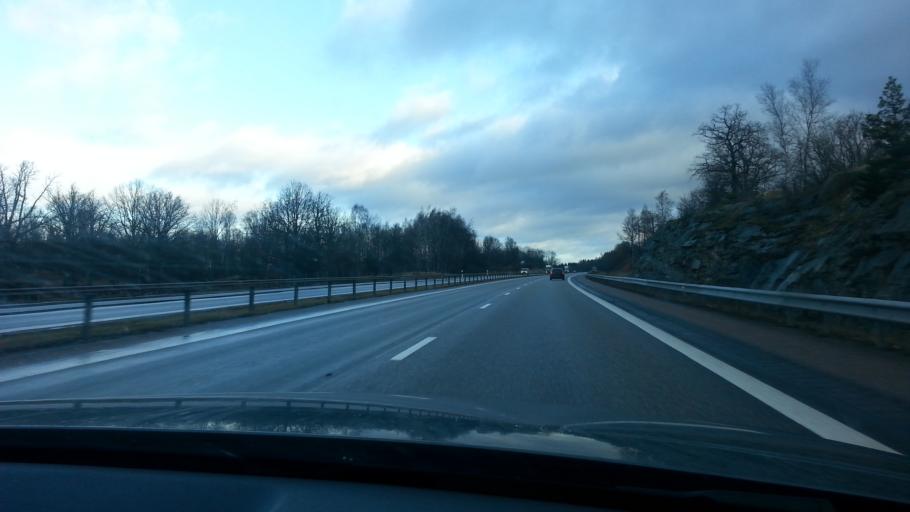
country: SE
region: OEstergoetland
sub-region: Odeshogs Kommun
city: OEdeshoeg
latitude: 58.1755
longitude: 14.5906
